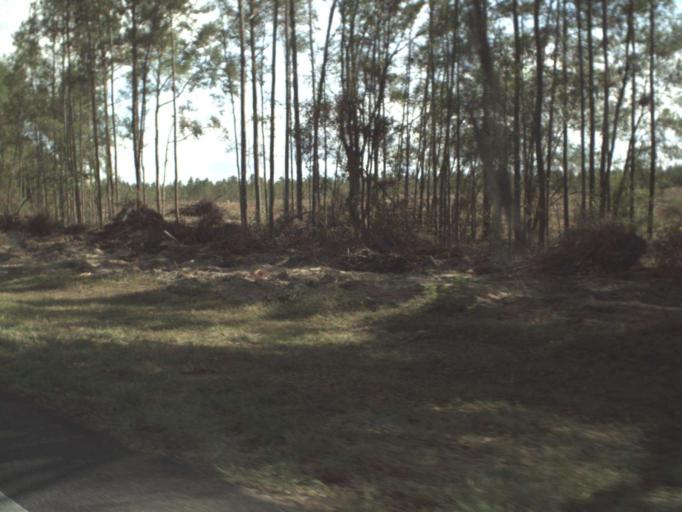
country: US
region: Florida
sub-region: Leon County
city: Woodville
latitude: 30.4191
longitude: -84.0934
